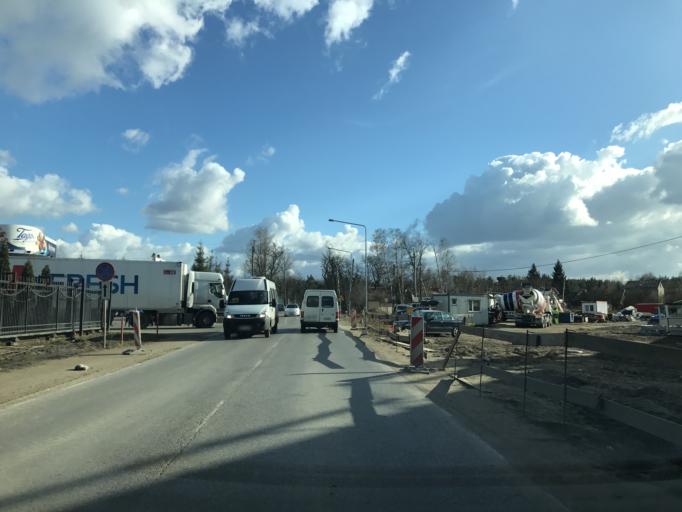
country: PL
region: Masovian Voivodeship
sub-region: Powiat wolominski
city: Radzymin
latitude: 52.3927
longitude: 21.1987
